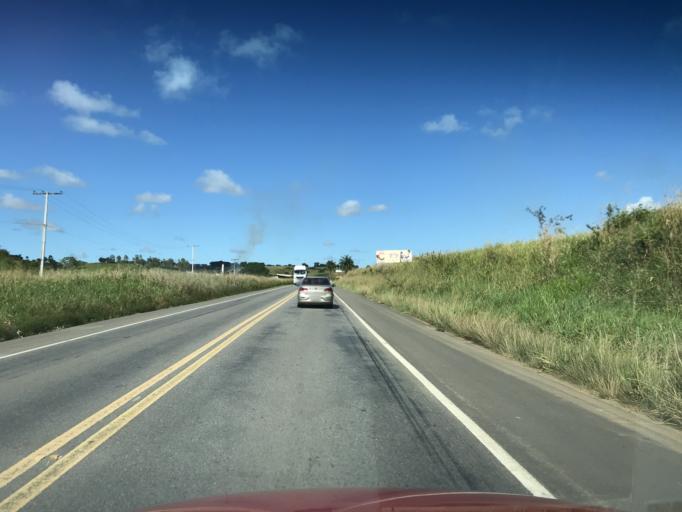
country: BR
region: Bahia
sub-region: Conceicao Do Almeida
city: Muritiba
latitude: -12.9418
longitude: -39.2514
